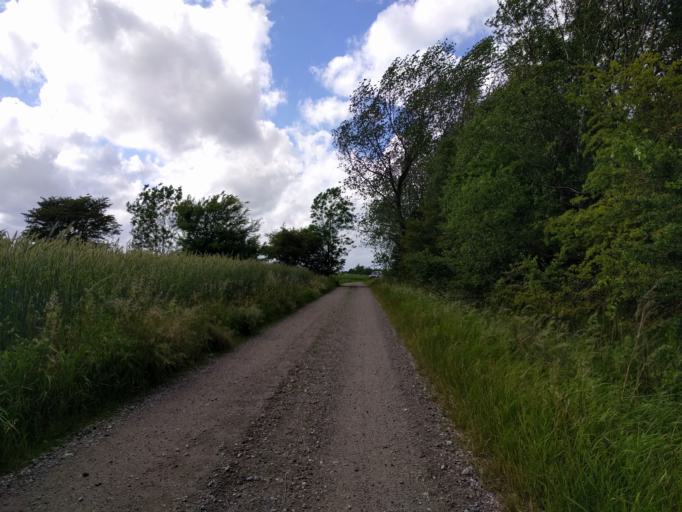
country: DK
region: South Denmark
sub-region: Kerteminde Kommune
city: Munkebo
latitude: 55.4651
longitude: 10.5142
